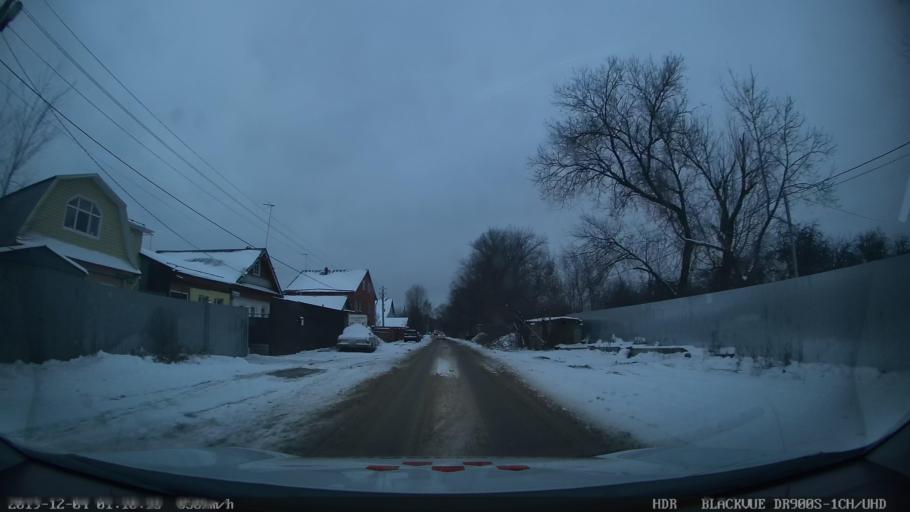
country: RU
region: Tatarstan
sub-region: Gorod Kazan'
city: Kazan
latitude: 55.8729
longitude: 49.0979
